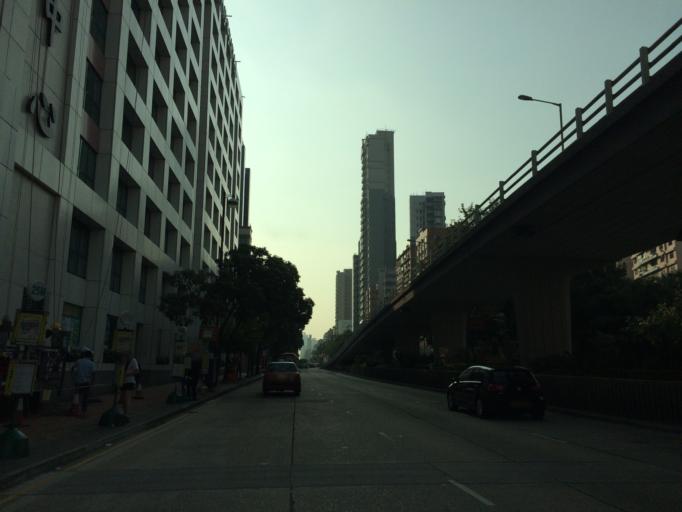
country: HK
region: Kowloon City
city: Kowloon
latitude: 22.3269
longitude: 114.1852
